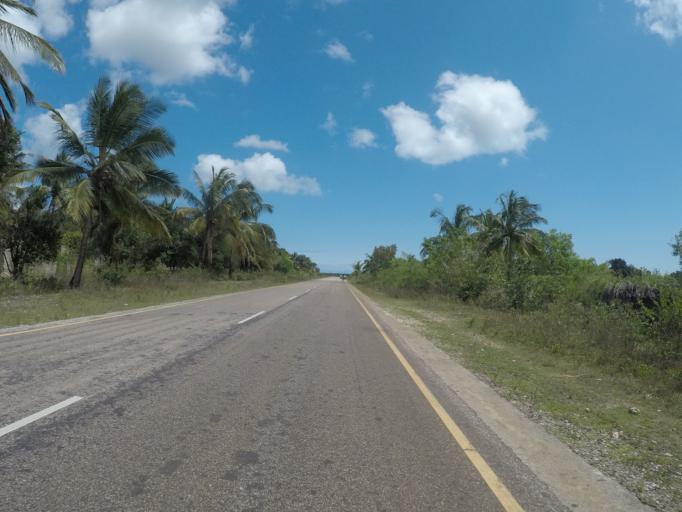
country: TZ
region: Zanzibar Central/South
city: Koani
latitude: -6.2453
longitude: 39.3557
